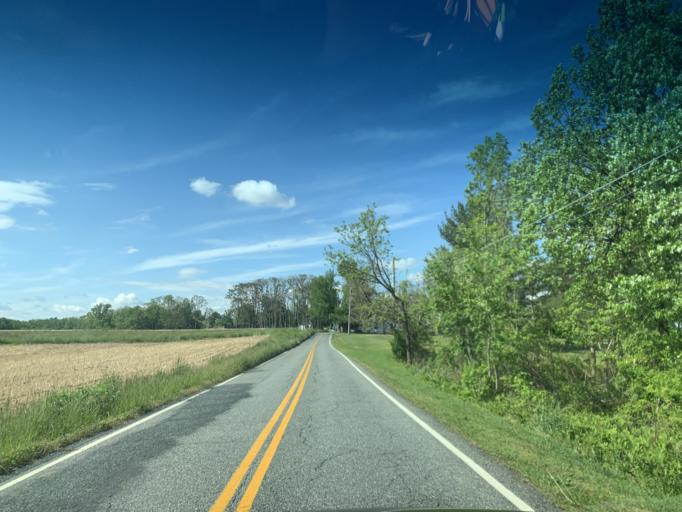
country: US
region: Maryland
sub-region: Cecil County
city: Rising Sun
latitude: 39.7112
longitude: -76.2024
